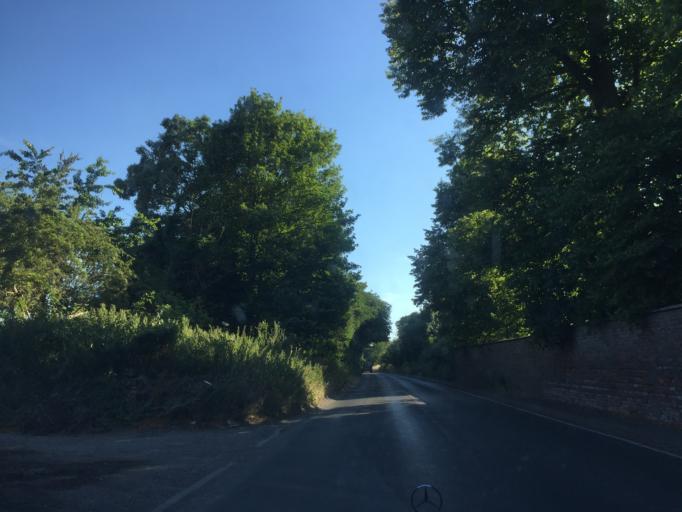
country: GB
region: England
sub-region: Oxfordshire
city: Watlington
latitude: 51.6568
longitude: -0.9915
